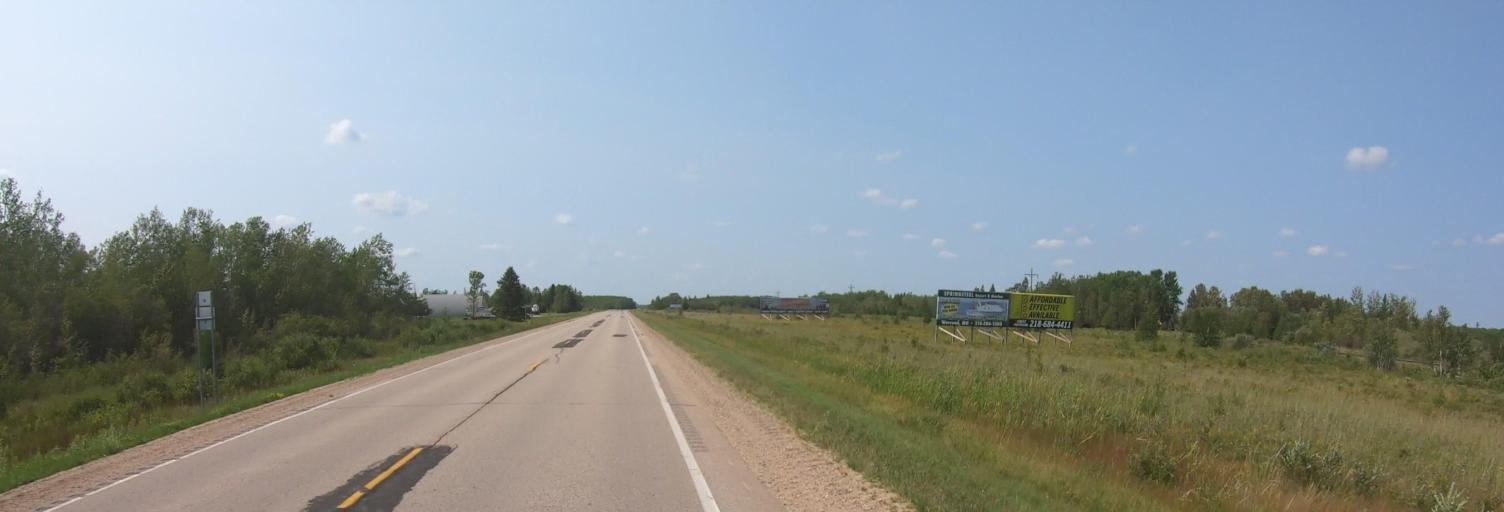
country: US
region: Minnesota
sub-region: Lake of the Woods County
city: Baudette
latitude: 48.7410
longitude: -94.8428
